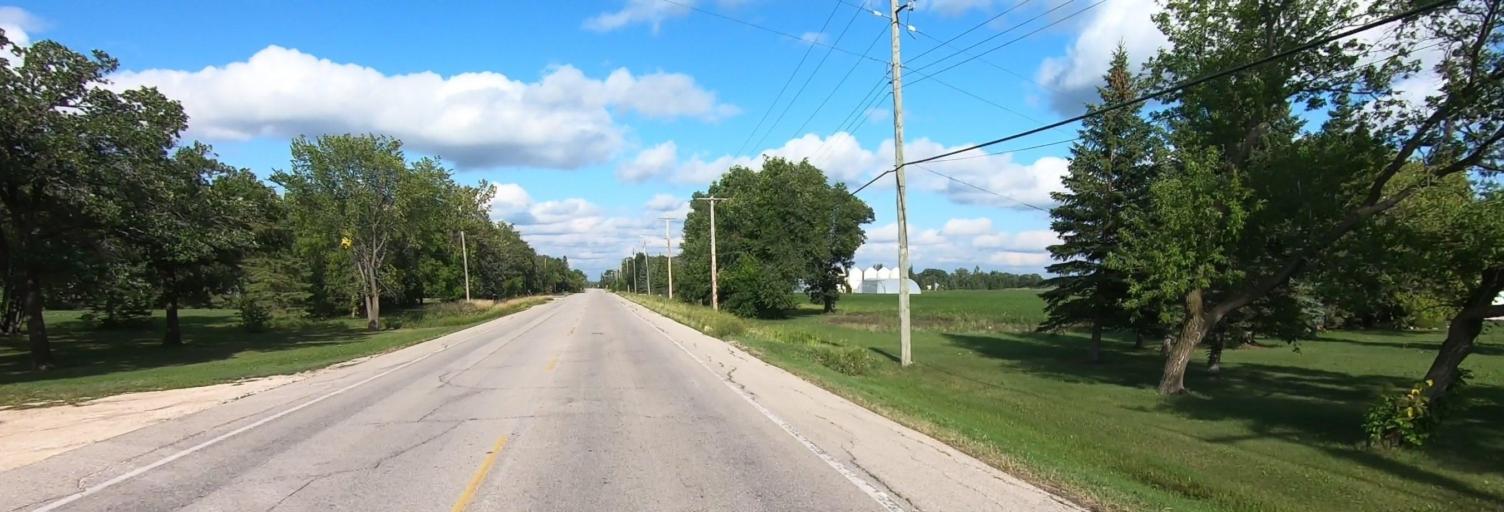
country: CA
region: Manitoba
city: Selkirk
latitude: 50.0345
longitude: -96.9953
